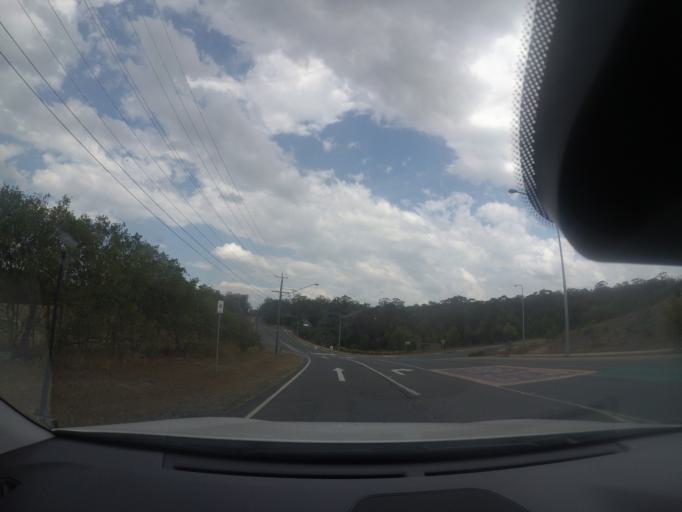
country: AU
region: Queensland
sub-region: Logan
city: Woodridge
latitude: -27.6204
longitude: 153.0931
